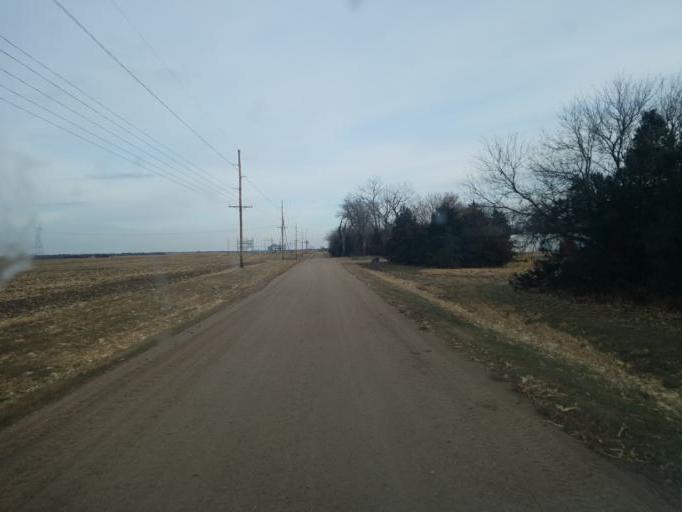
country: US
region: Nebraska
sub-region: Holt County
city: O'Neill
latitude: 42.4369
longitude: -98.3222
